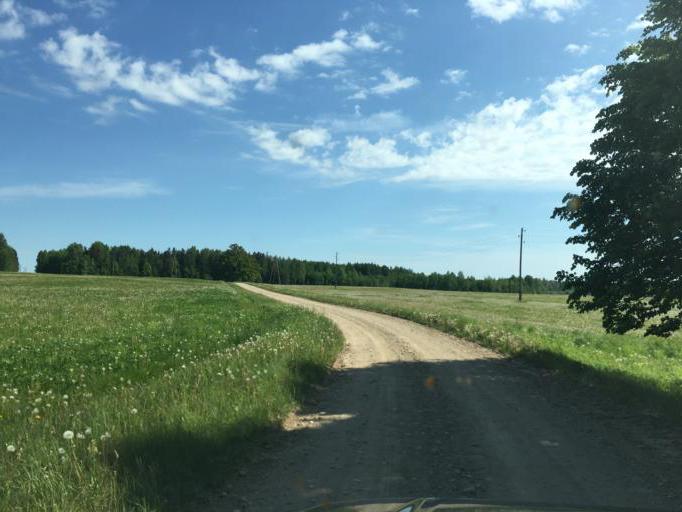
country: LV
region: Talsu Rajons
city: Talsi
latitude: 57.3151
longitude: 22.4418
